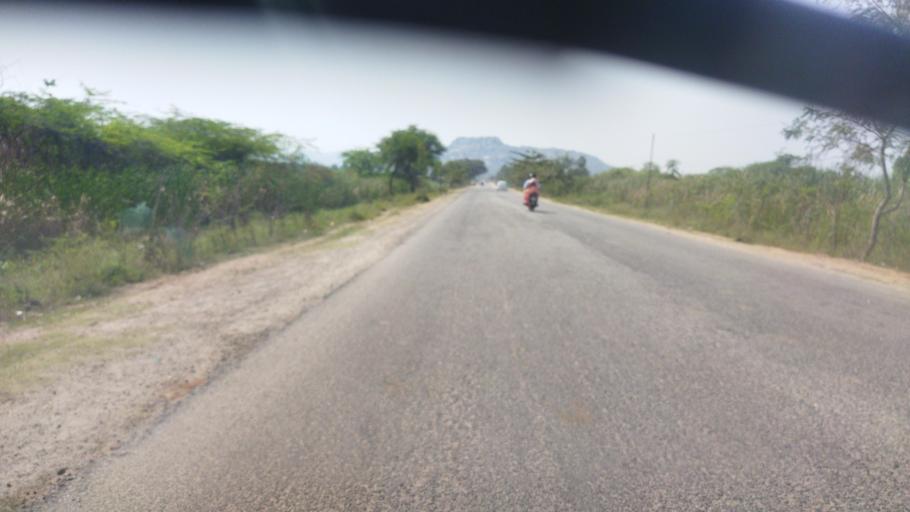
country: IN
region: Telangana
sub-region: Nalgonda
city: Nalgonda
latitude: 17.1171
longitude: 79.2836
